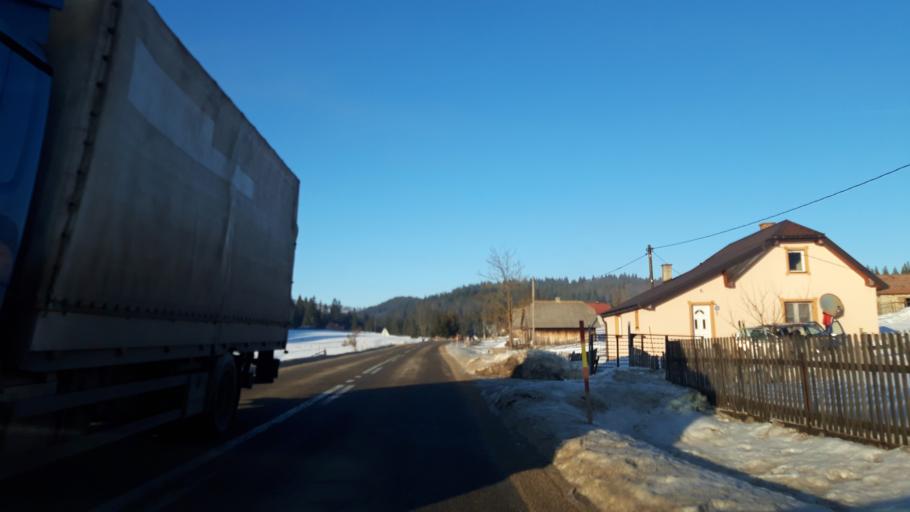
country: BA
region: Republika Srpska
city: Han Pijesak
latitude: 44.1109
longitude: 18.9684
